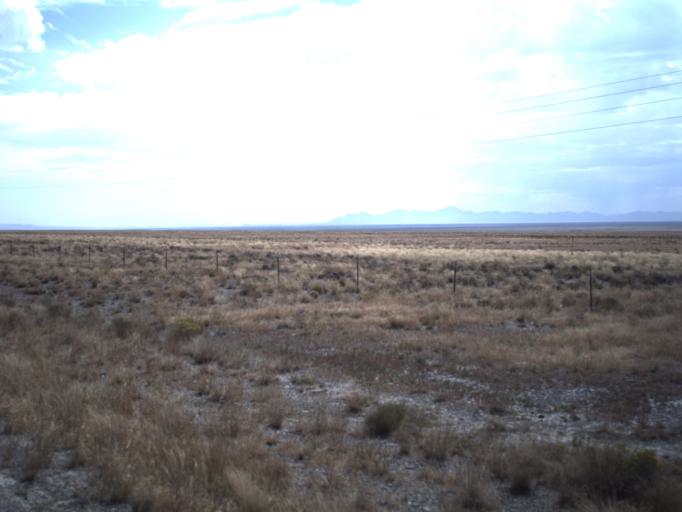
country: US
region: Utah
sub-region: Tooele County
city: Wendover
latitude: 41.4299
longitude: -113.8090
